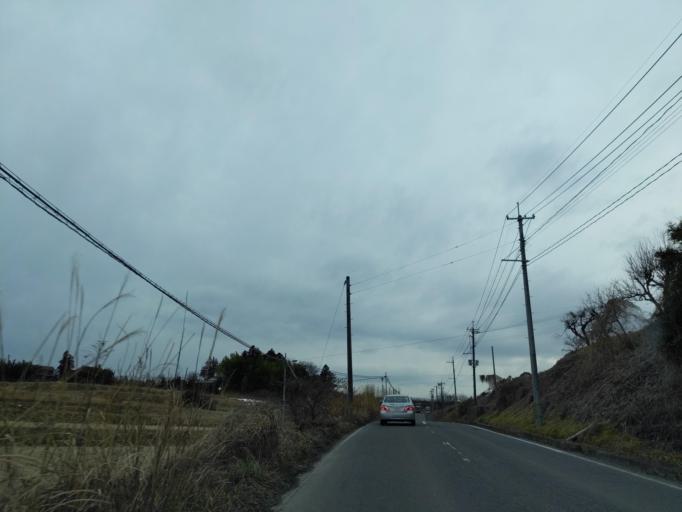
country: JP
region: Fukushima
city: Motomiya
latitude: 37.4562
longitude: 140.4045
